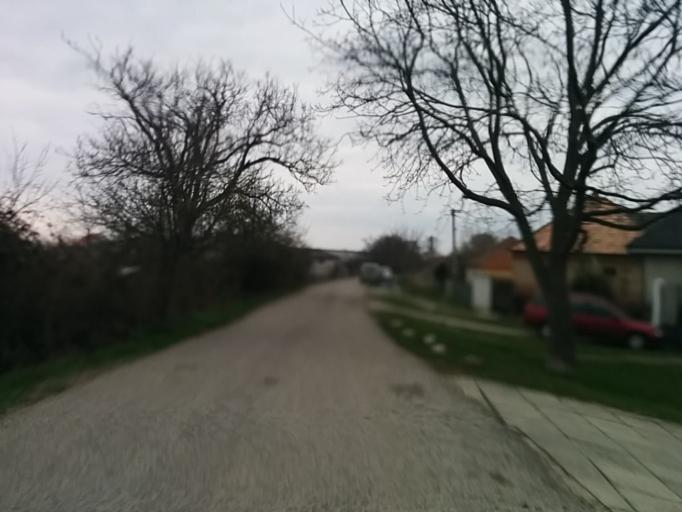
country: SK
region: Nitriansky
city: Sellye
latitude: 48.2447
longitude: 17.8257
